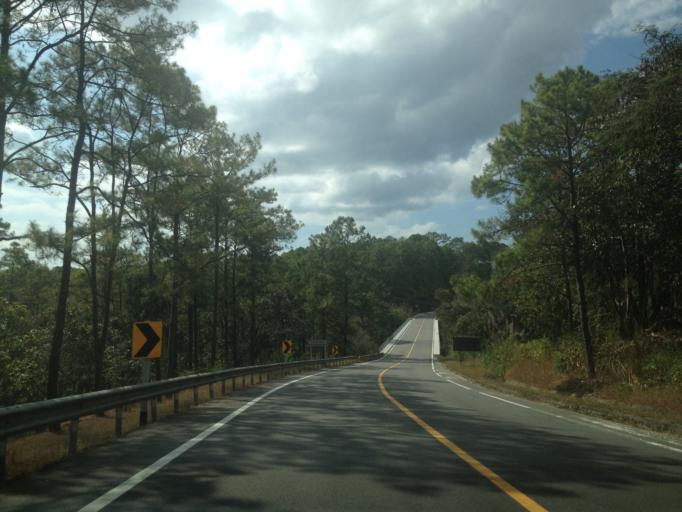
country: TH
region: Mae Hong Son
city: Pa Pae
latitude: 18.1502
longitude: 98.2969
